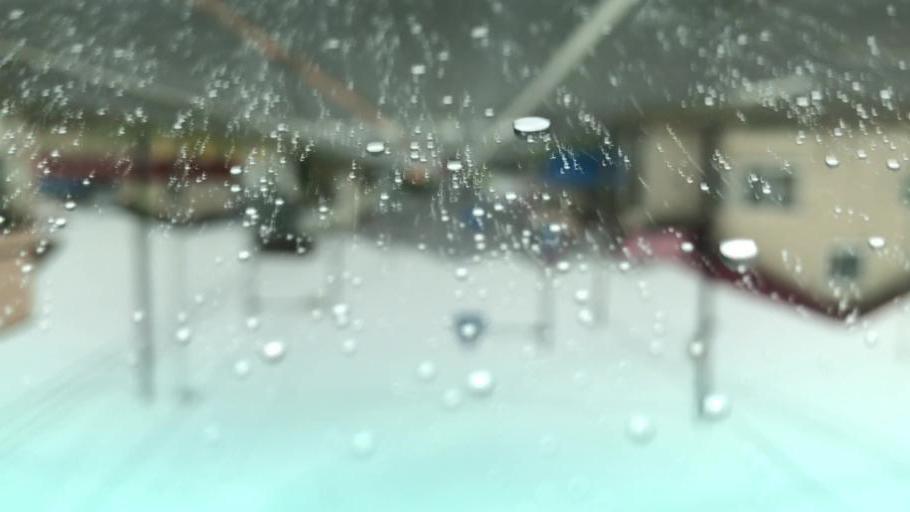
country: JP
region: Hokkaido
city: Shizunai-furukawacho
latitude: 42.2678
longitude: 142.4991
